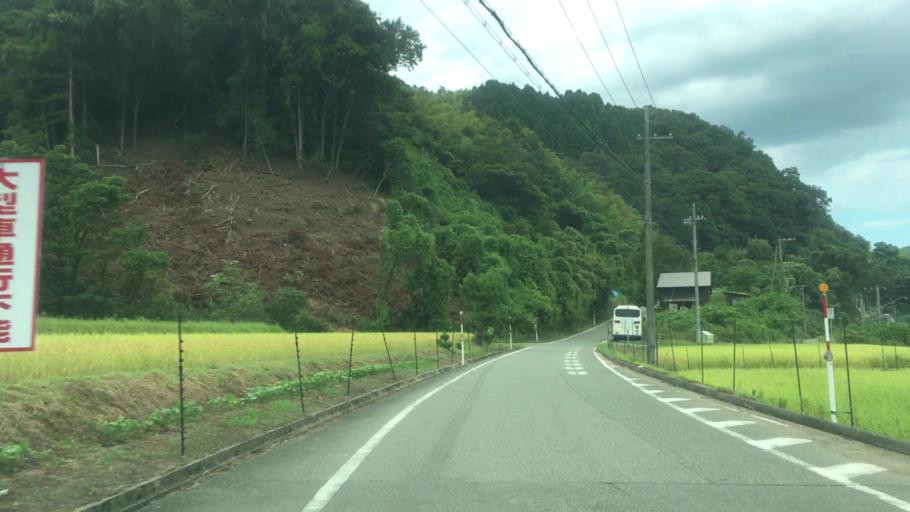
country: JP
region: Hyogo
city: Toyooka
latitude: 35.5806
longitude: 134.7995
